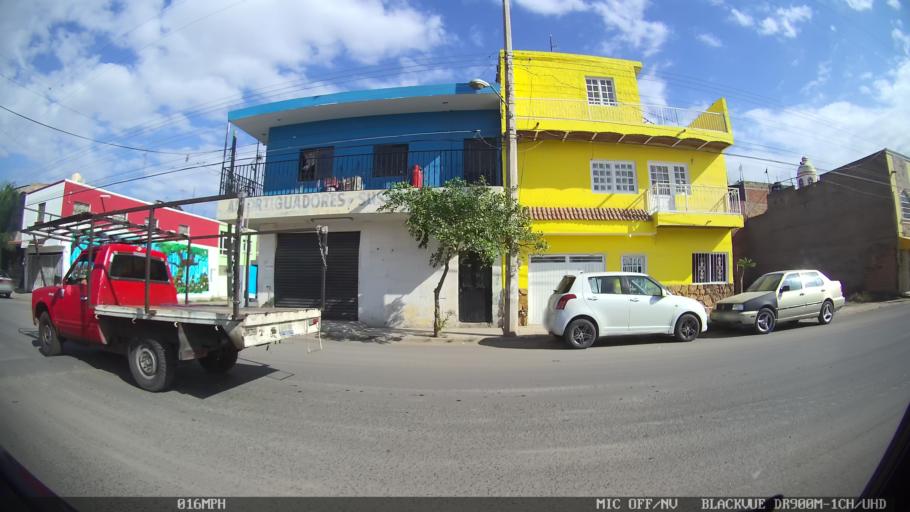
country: MX
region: Jalisco
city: Tonala
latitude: 20.6543
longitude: -103.2482
